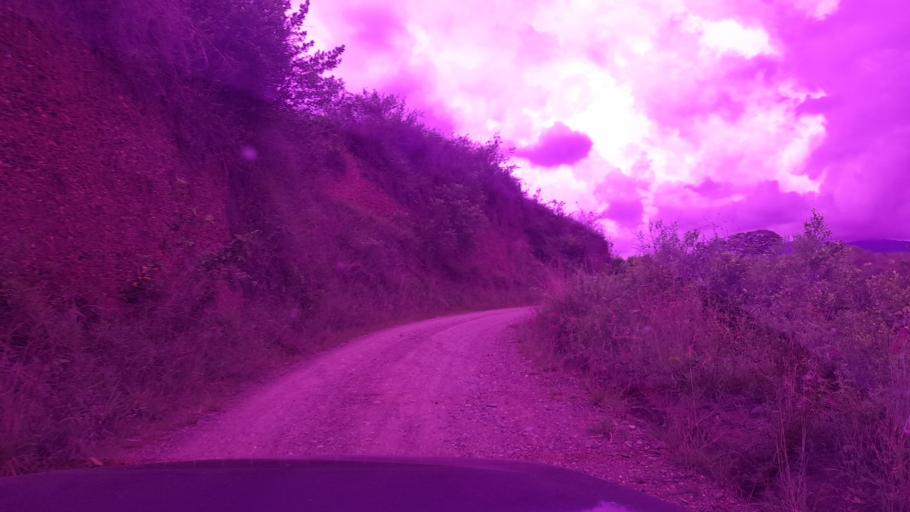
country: CO
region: Valle del Cauca
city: Andalucia
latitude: 4.1697
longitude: -76.1193
